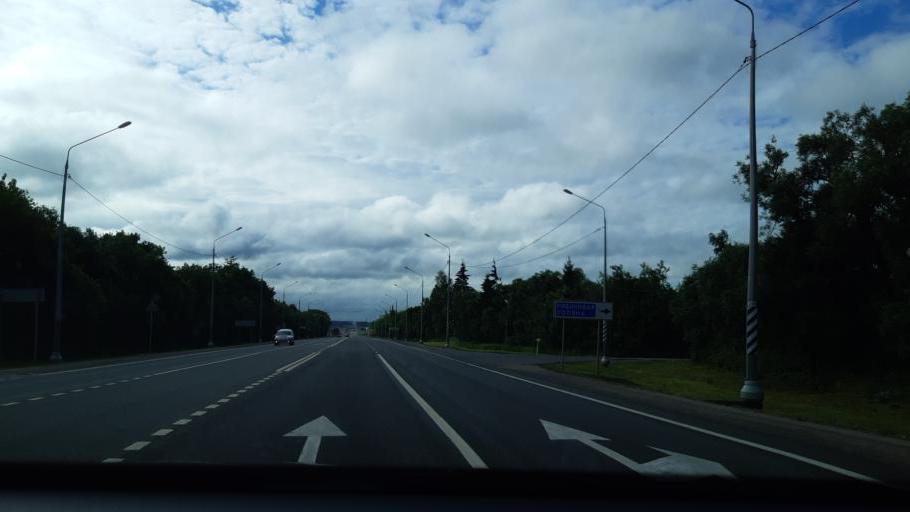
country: RU
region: Smolensk
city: Smolensk
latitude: 54.7162
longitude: 32.1080
